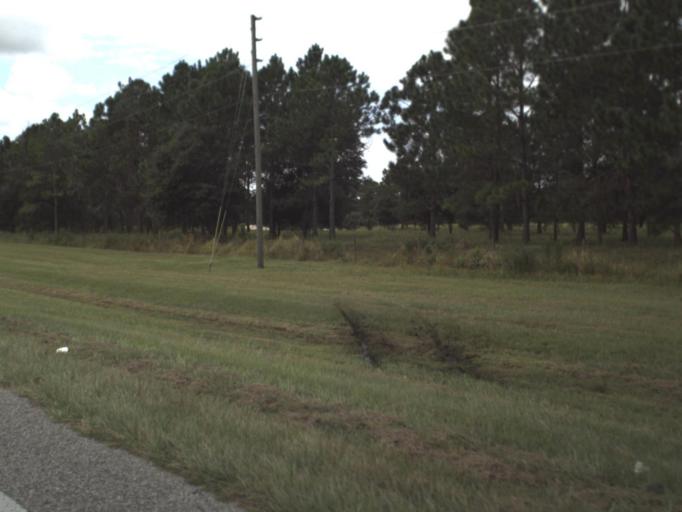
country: US
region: Florida
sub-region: Hardee County
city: Bowling Green
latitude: 27.6907
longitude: -81.8127
